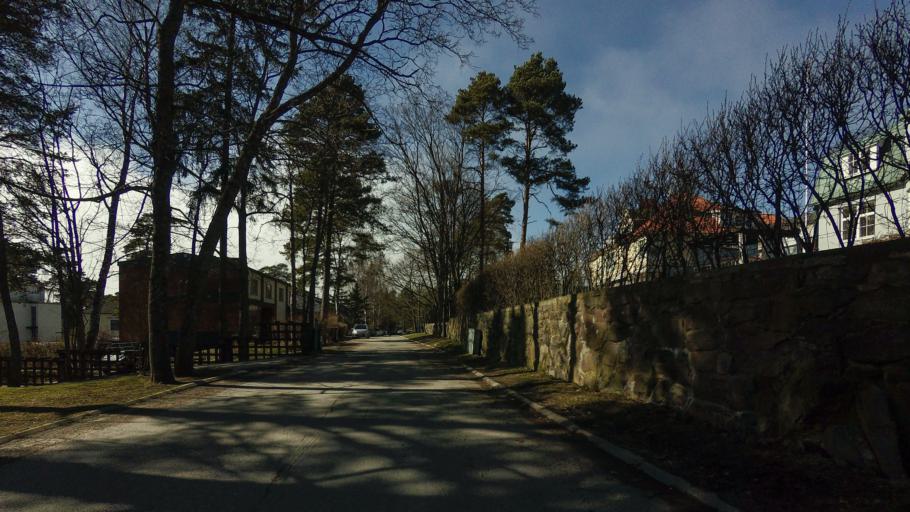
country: FI
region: Uusimaa
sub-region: Helsinki
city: Helsinki
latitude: 60.1802
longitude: 25.0133
